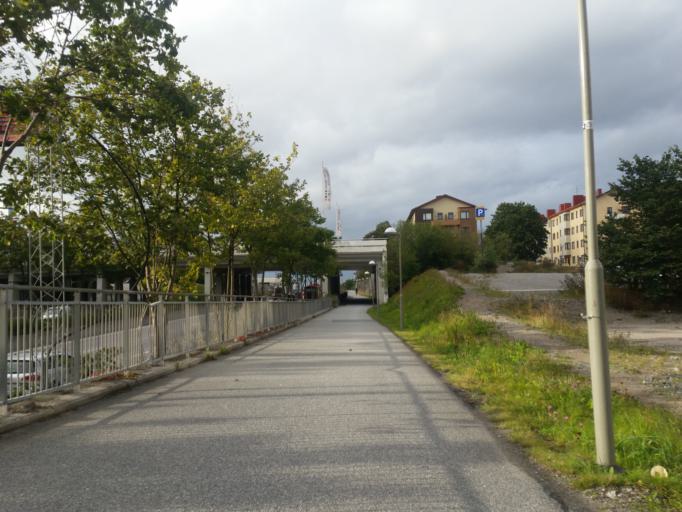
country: SE
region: Stockholm
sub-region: Stockholms Kommun
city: Arsta
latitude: 59.2935
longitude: 18.0858
